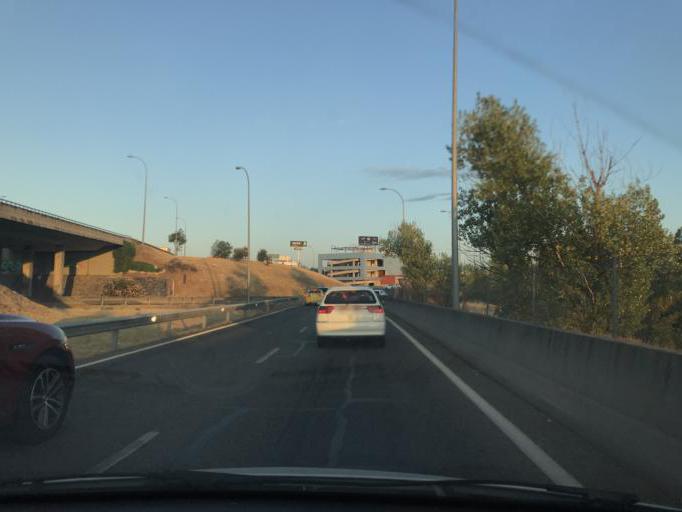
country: ES
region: Madrid
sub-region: Provincia de Madrid
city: Alcobendas
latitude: 40.5333
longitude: -3.6382
